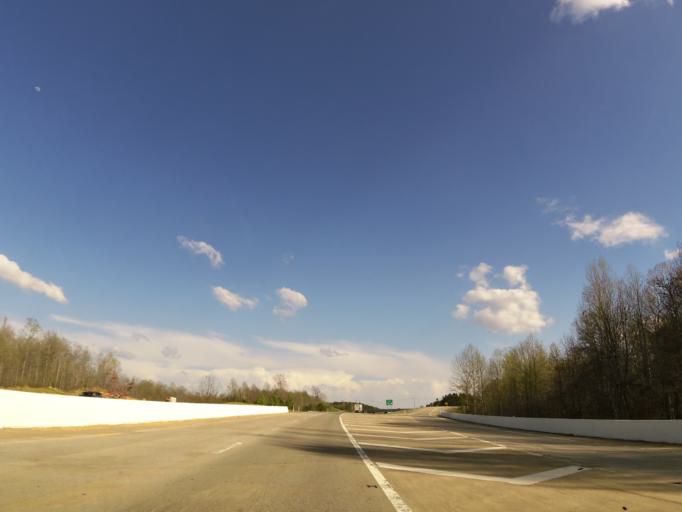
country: US
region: Tennessee
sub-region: Williamson County
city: Fairview
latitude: 35.8821
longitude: -87.1021
